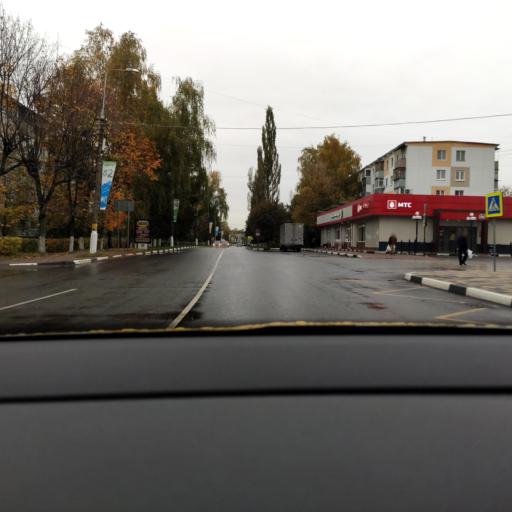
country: RU
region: Moskovskaya
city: Ivanteyevka
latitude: 55.9677
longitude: 37.9073
